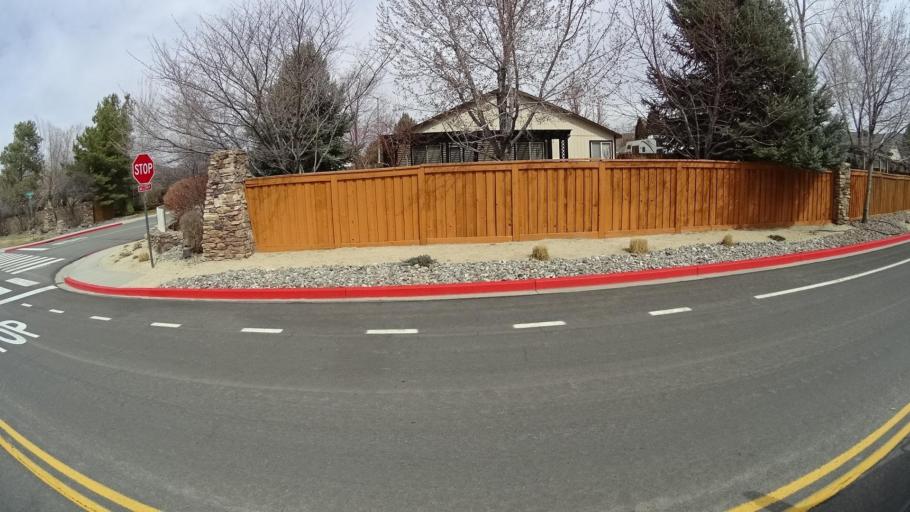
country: US
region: Nevada
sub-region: Washoe County
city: Spanish Springs
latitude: 39.6263
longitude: -119.6832
